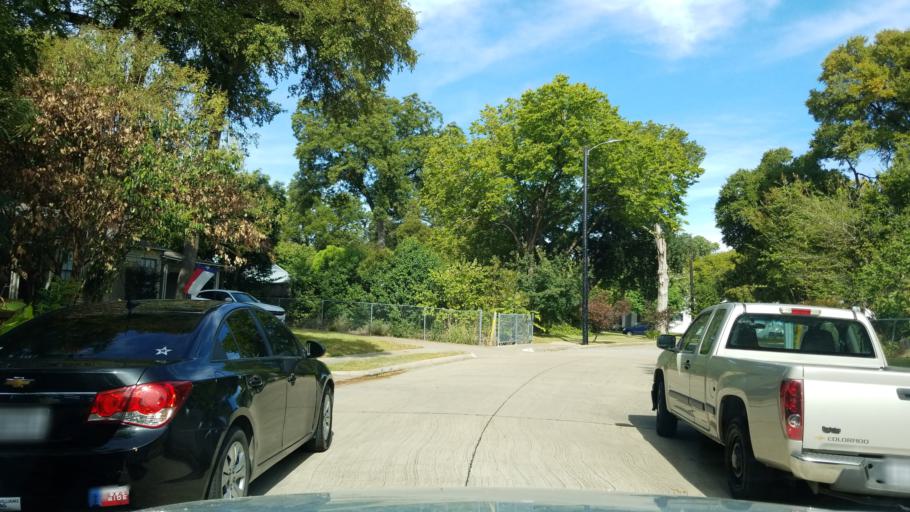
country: US
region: Texas
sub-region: Dallas County
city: Garland
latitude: 32.9040
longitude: -96.6508
